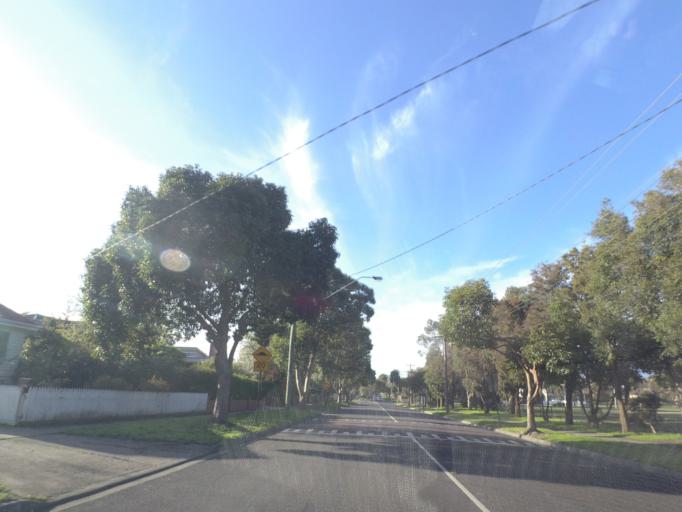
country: AU
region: Victoria
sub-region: Whitehorse
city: Box Hill North
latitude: -37.8094
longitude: 145.1324
